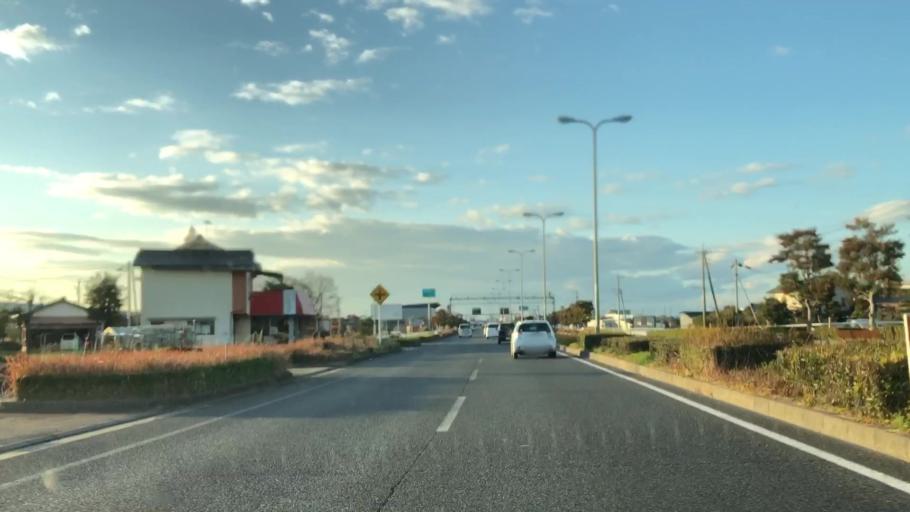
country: JP
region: Fukuoka
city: Nakatsu
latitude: 33.5445
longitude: 131.2859
